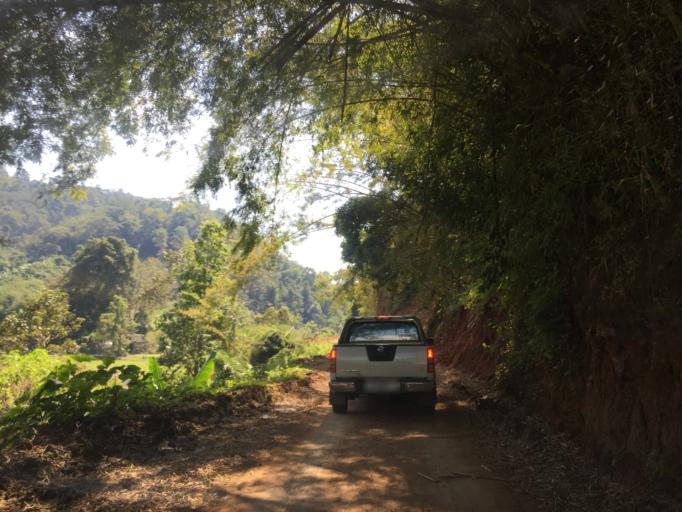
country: TH
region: Chiang Mai
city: Samoeng
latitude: 19.0058
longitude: 98.7299
